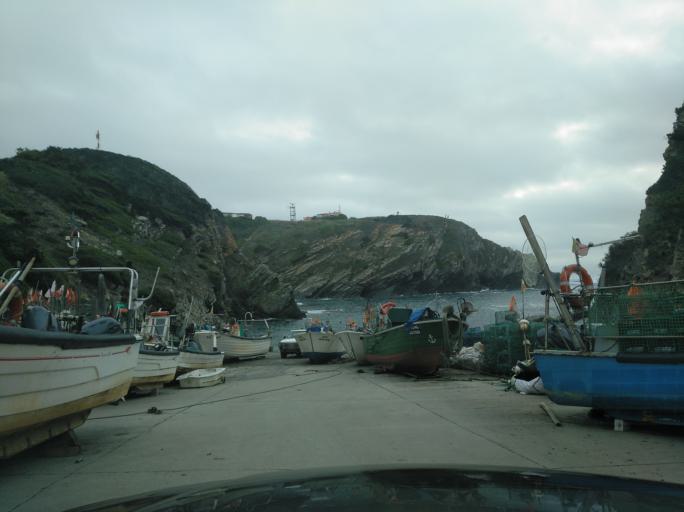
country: PT
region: Beja
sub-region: Odemira
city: Sao Teotonio
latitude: 37.5524
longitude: -8.7919
